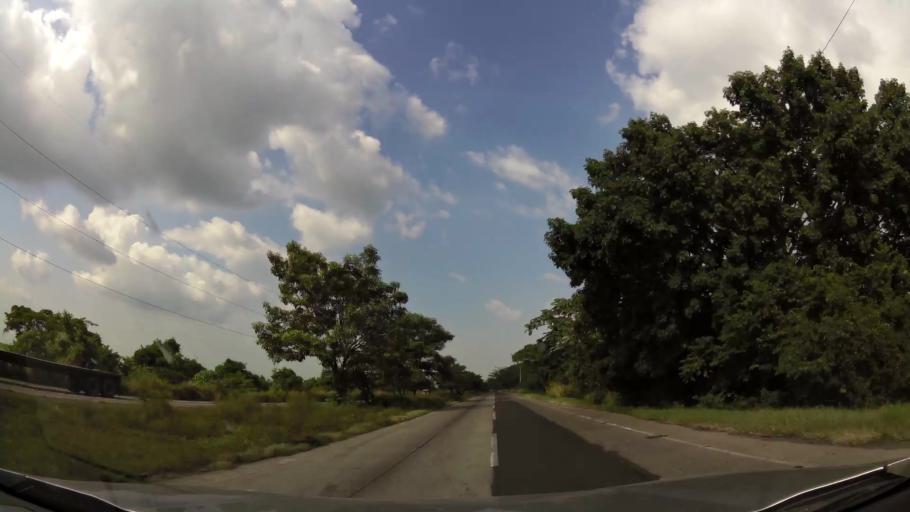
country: GT
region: Escuintla
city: Puerto San Jose
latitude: 14.0476
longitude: -90.7773
